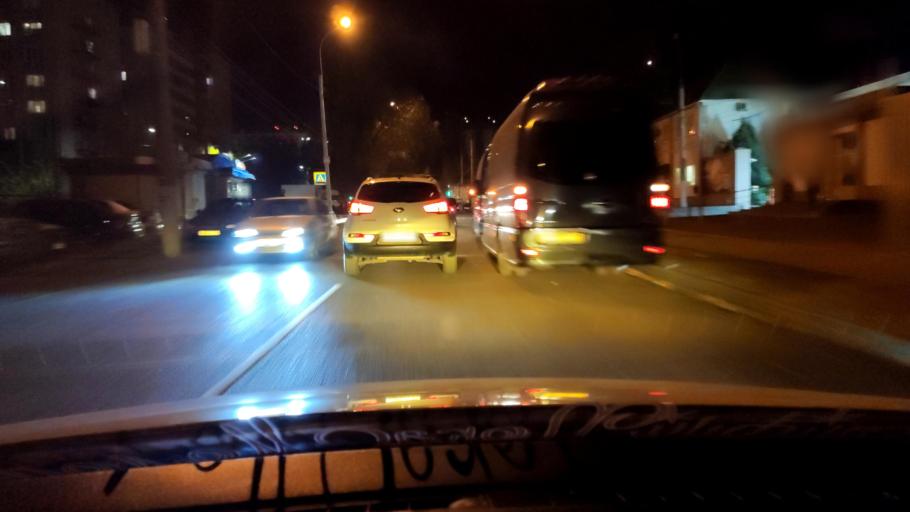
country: RU
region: Voronezj
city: Podgornoye
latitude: 51.6912
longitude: 39.1352
